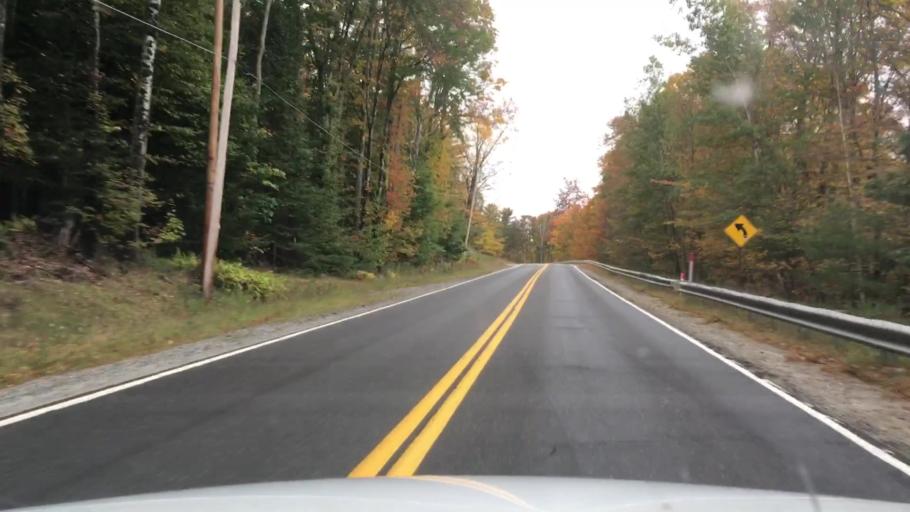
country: US
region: Maine
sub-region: Oxford County
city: Bethel
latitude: 44.4051
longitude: -70.7976
